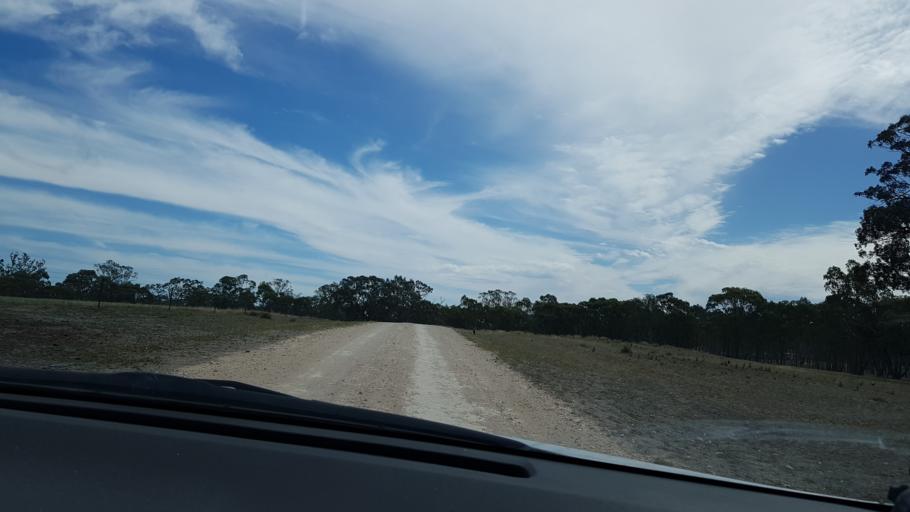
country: AU
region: Victoria
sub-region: Horsham
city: Horsham
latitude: -36.6852
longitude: 141.7781
